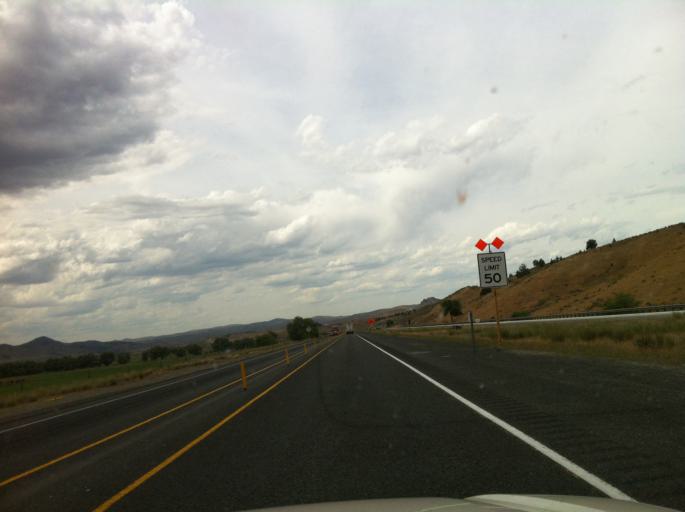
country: US
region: Oregon
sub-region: Baker County
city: Baker City
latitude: 44.5482
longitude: -117.4212
